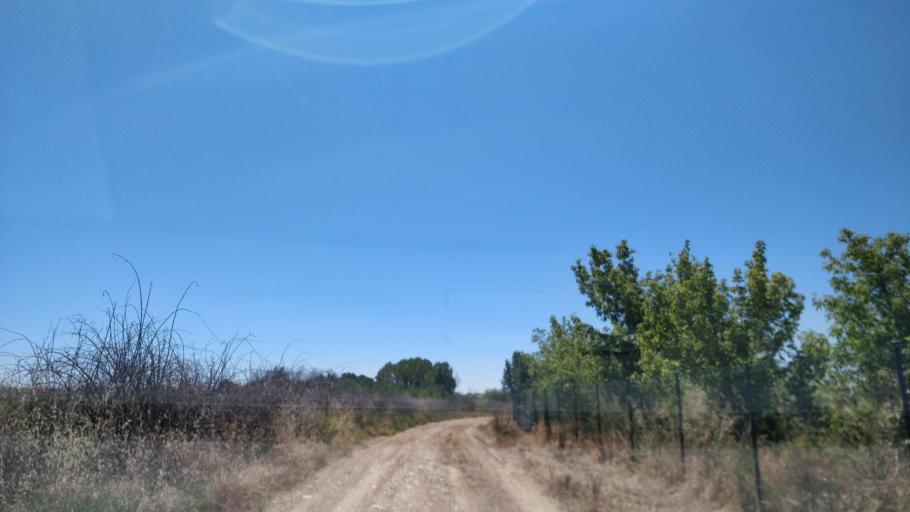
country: ES
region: Castille and Leon
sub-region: Provincia de Leon
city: Bustillo del Paramo
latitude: 42.4800
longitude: -5.8069
